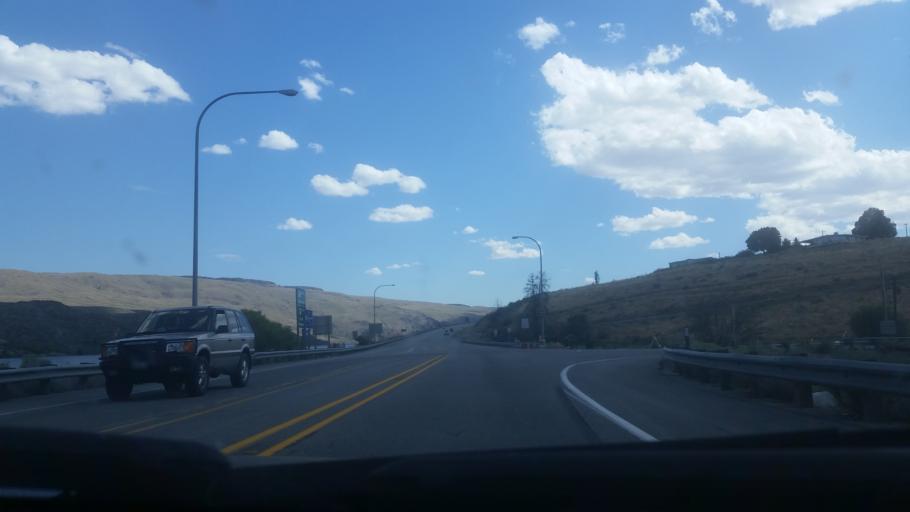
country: US
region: Washington
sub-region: Okanogan County
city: Brewster
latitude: 48.0488
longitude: -119.9019
